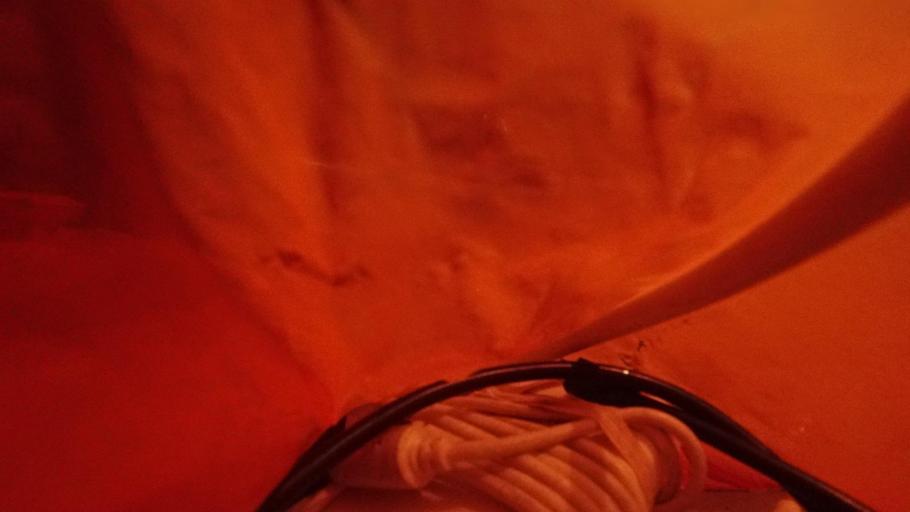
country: RU
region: Jewish Autonomous Oblast
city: Khingansk
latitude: 49.1639
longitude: 130.7634
